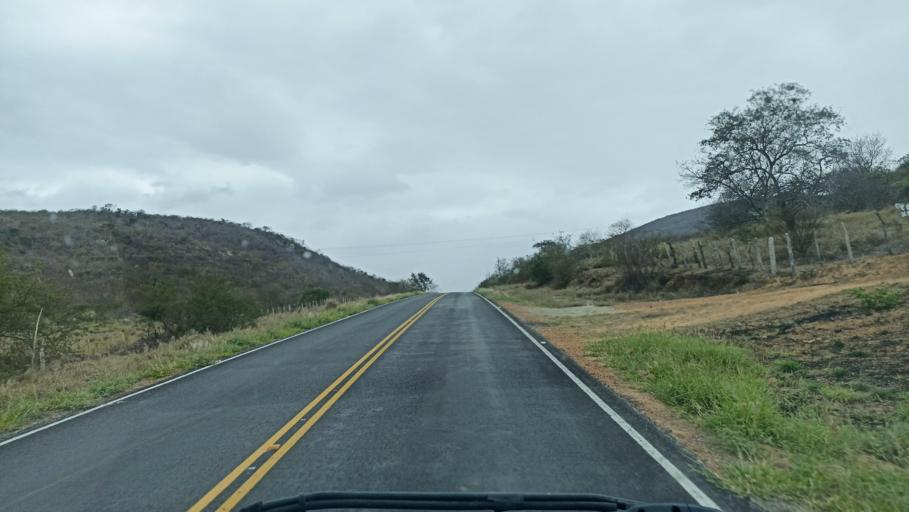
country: BR
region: Bahia
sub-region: Andarai
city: Vera Cruz
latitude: -13.0466
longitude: -40.7764
